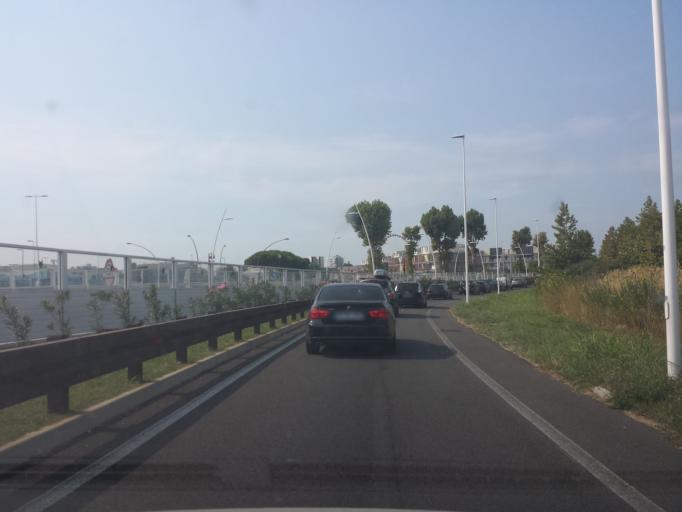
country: IT
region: Veneto
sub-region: Provincia di Venezia
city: Lido di Iesolo
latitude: 45.5087
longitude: 12.6346
